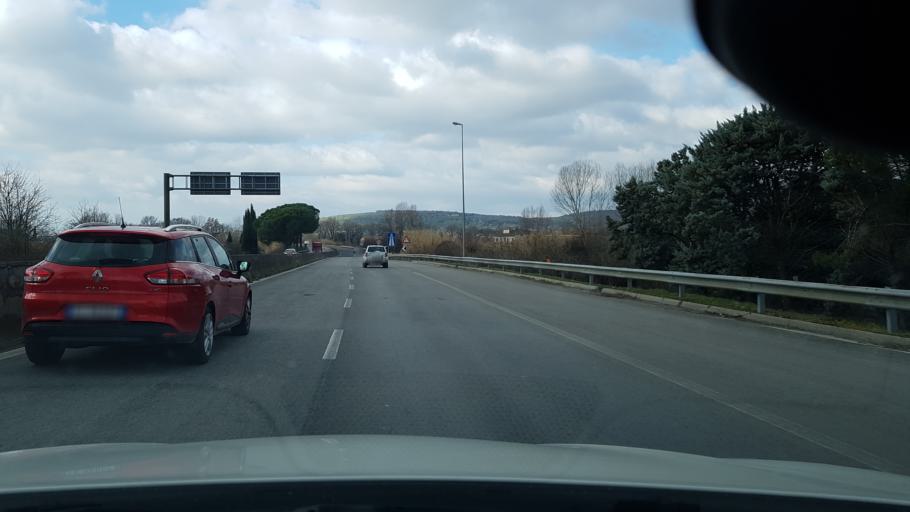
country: IT
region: Umbria
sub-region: Provincia di Perugia
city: Tuoro sul Trasimeno
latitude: 43.1973
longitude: 12.0768
